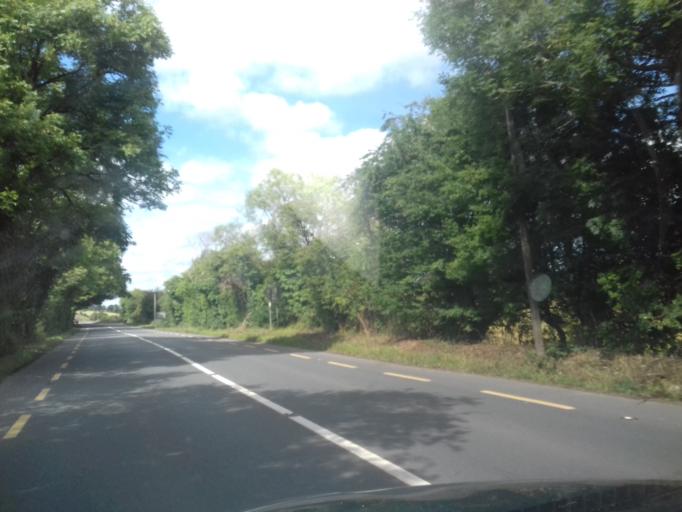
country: IE
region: Leinster
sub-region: Wicklow
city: Valleymount
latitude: 53.0382
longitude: -6.6355
